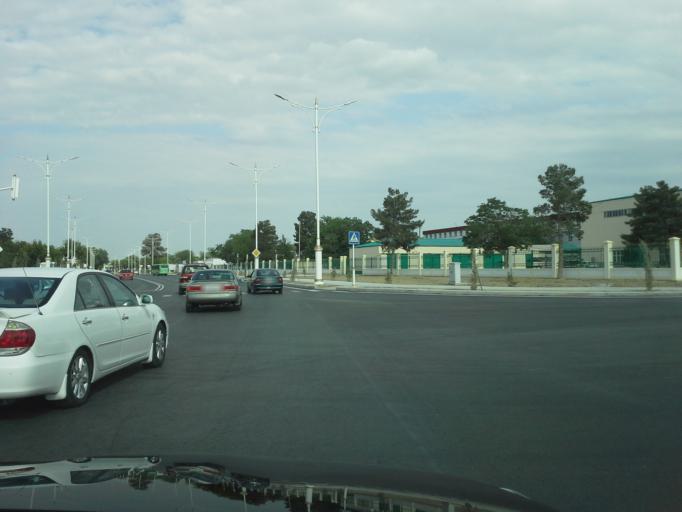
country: TM
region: Ahal
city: Ashgabat
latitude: 37.9584
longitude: 58.3395
